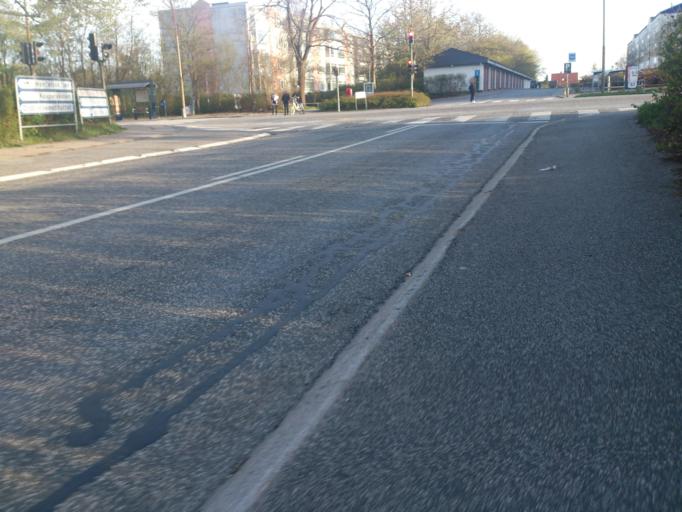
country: DK
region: Capital Region
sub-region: Ballerup Kommune
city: Ballerup
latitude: 55.7294
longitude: 12.3507
